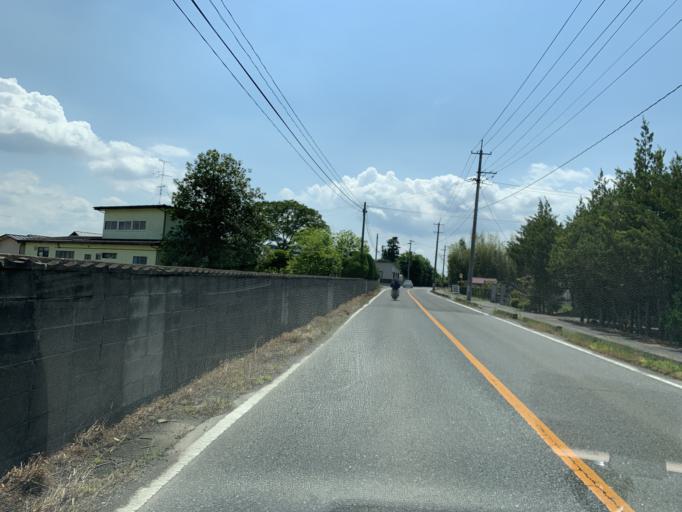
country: JP
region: Miyagi
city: Kogota
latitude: 38.5742
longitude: 141.0362
